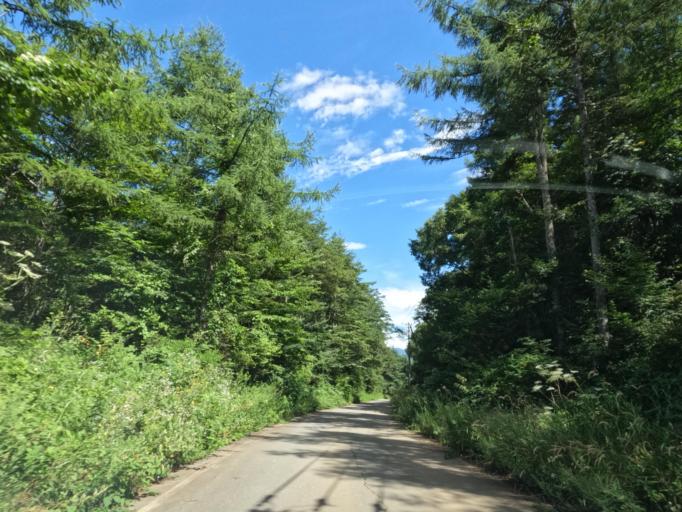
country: JP
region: Yamanashi
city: Nirasaki
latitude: 35.9447
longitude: 138.4550
